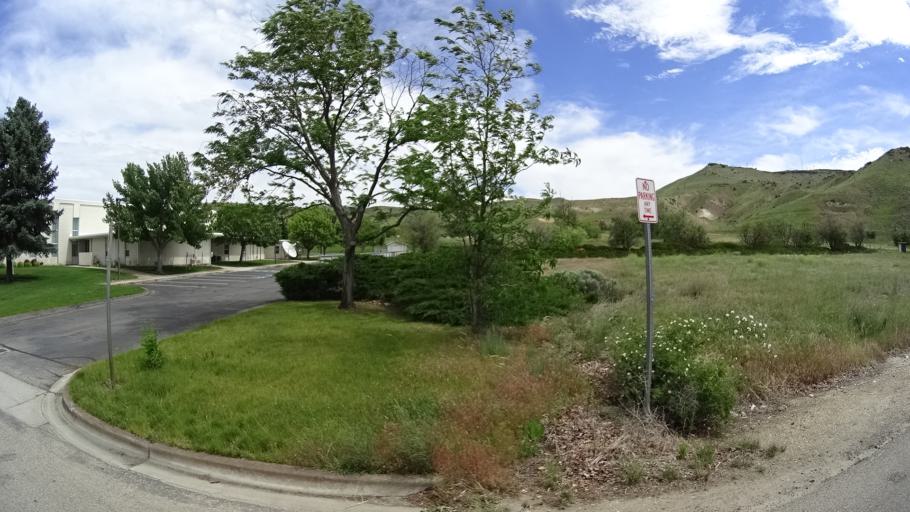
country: US
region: Idaho
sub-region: Ada County
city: Boise
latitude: 43.5979
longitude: -116.1646
